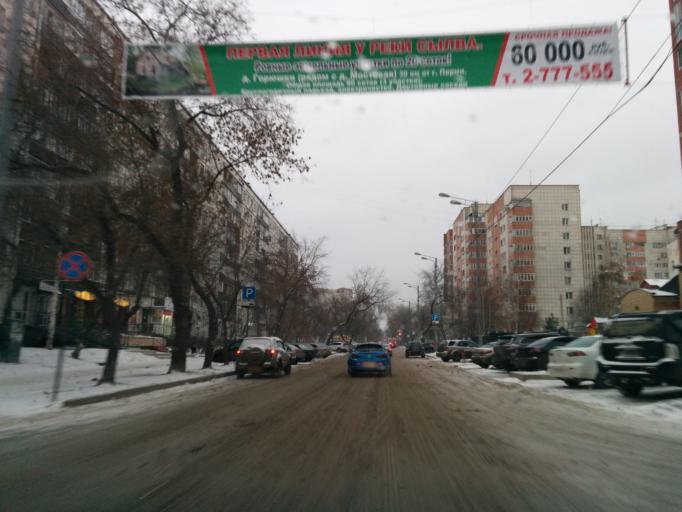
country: RU
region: Perm
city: Perm
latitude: 58.0034
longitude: 56.2186
